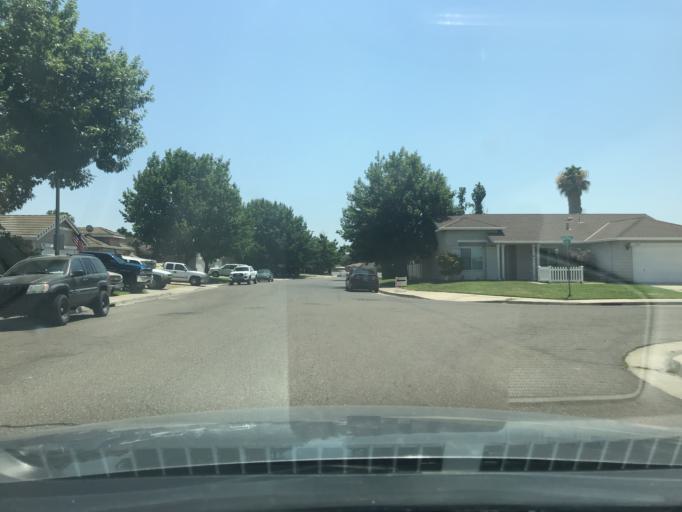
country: US
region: California
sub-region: Merced County
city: Atwater
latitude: 37.3517
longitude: -120.5807
